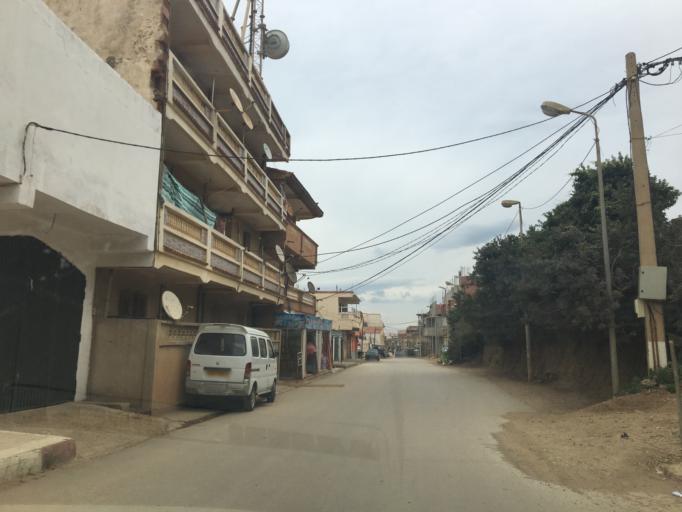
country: DZ
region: Tipaza
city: Tipasa
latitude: 36.6417
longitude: 2.3549
